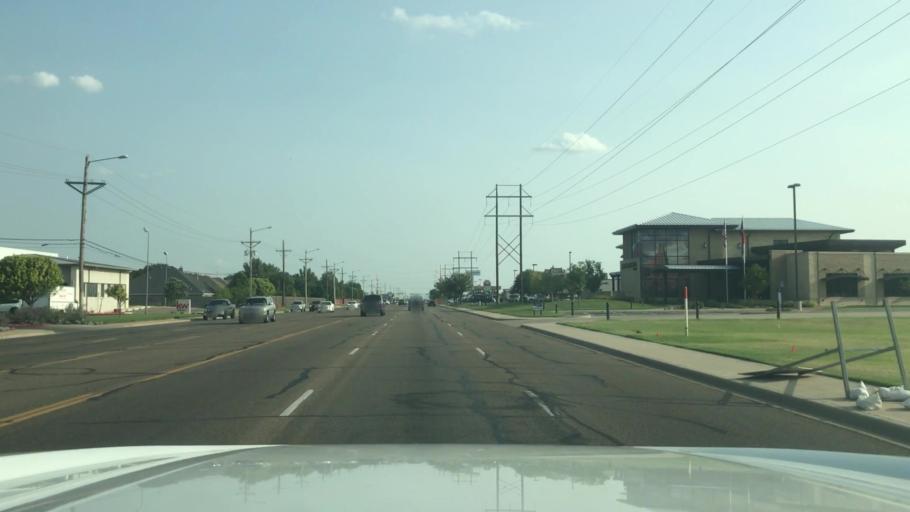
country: US
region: Texas
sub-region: Potter County
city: Amarillo
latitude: 35.1671
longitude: -101.9382
